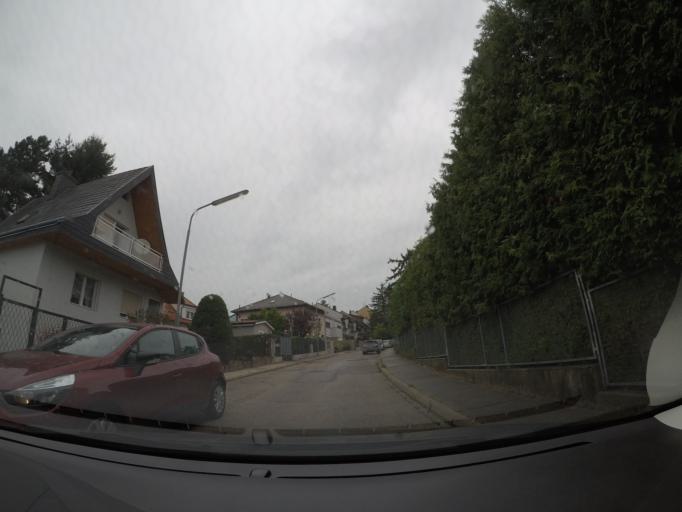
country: AT
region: Lower Austria
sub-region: Politischer Bezirk Modling
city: Perchtoldsdorf
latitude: 48.1688
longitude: 16.2596
